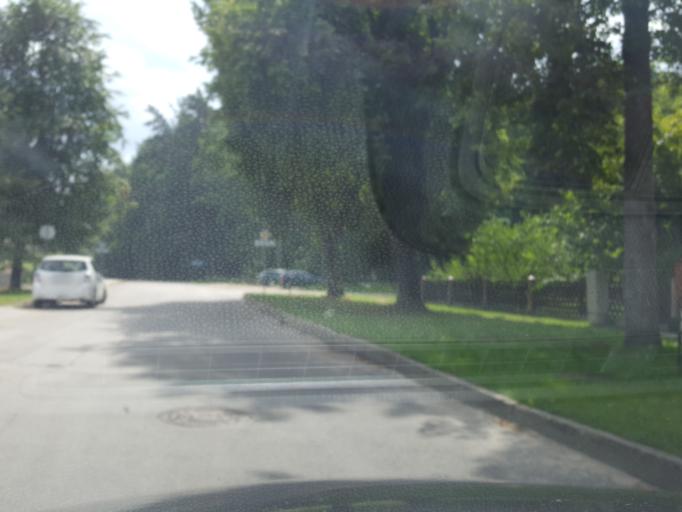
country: LT
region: Alytaus apskritis
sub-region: Alytus
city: Alytus
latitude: 54.3852
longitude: 24.0420
